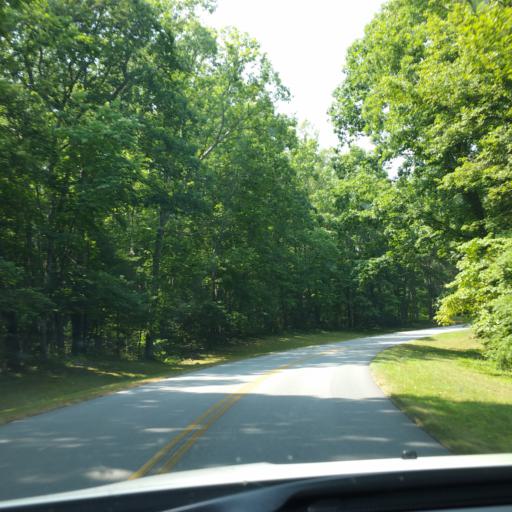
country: US
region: North Carolina
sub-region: Buncombe County
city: Avery Creek
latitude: 35.4990
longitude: -82.5579
